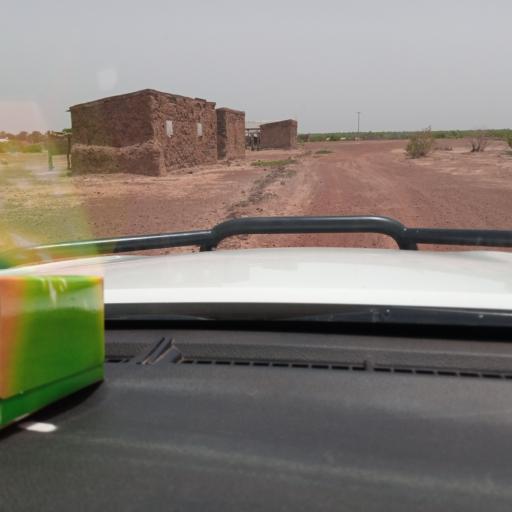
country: ML
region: Koulikoro
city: Koulikoro
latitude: 13.1085
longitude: -7.6128
